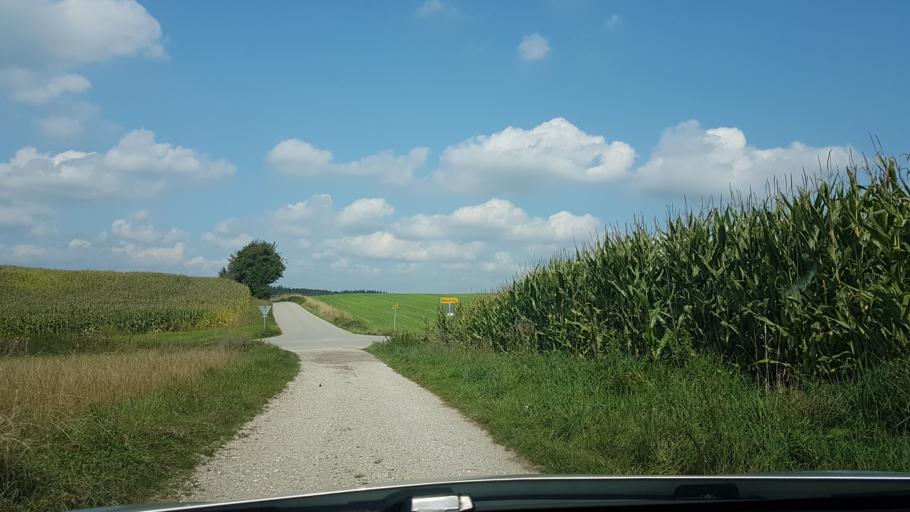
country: DE
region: Bavaria
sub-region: Upper Bavaria
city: Kirchberg
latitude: 48.3664
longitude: 12.0452
